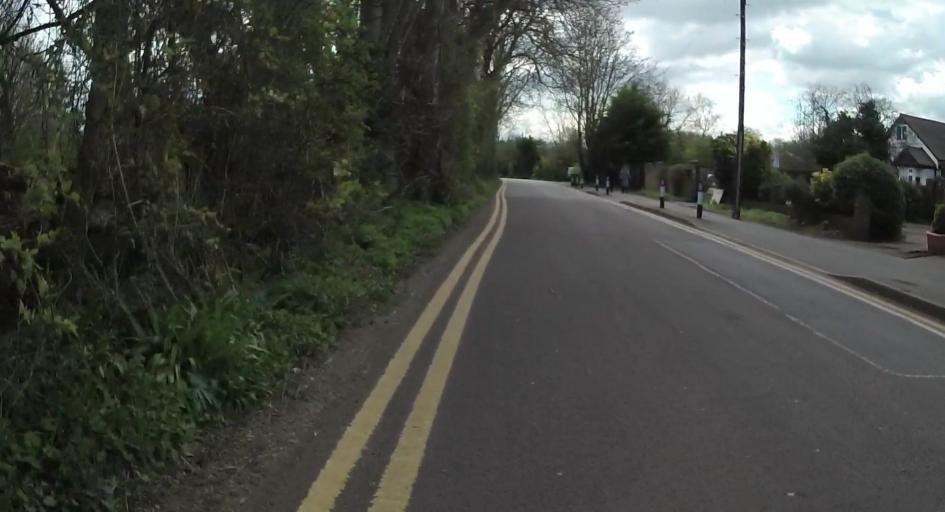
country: GB
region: England
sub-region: Surrey
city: Weybridge
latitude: 51.3849
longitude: -0.4581
